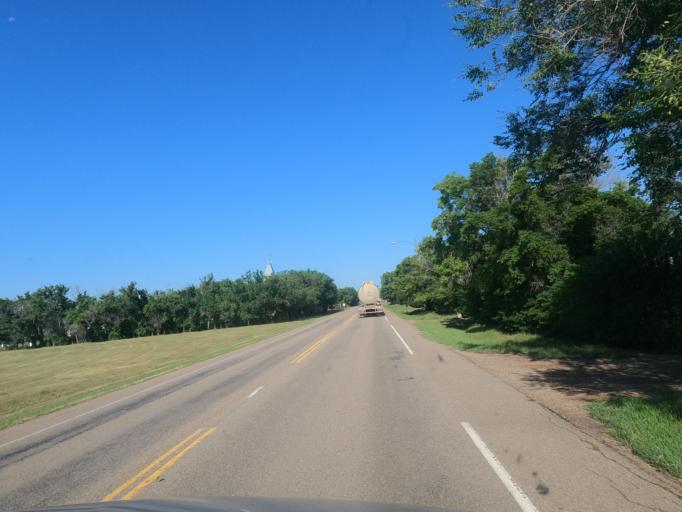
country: CA
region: Saskatchewan
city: Swift Current
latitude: 49.7278
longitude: -107.7372
